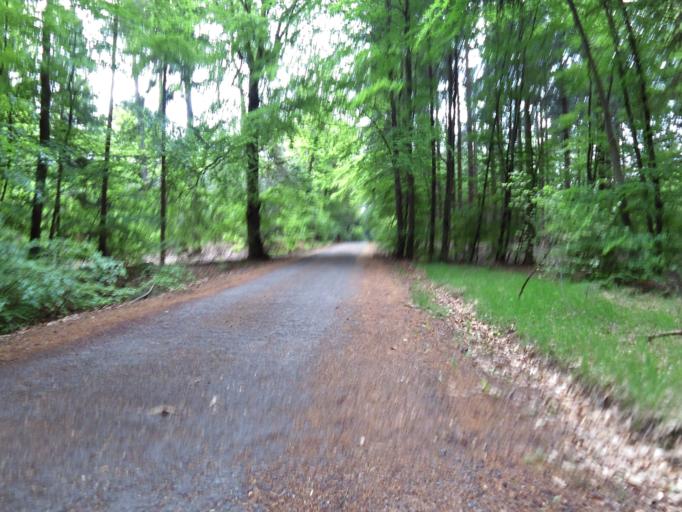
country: DE
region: Rheinland-Pfalz
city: Frankenstein
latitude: 49.4835
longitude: 7.9738
